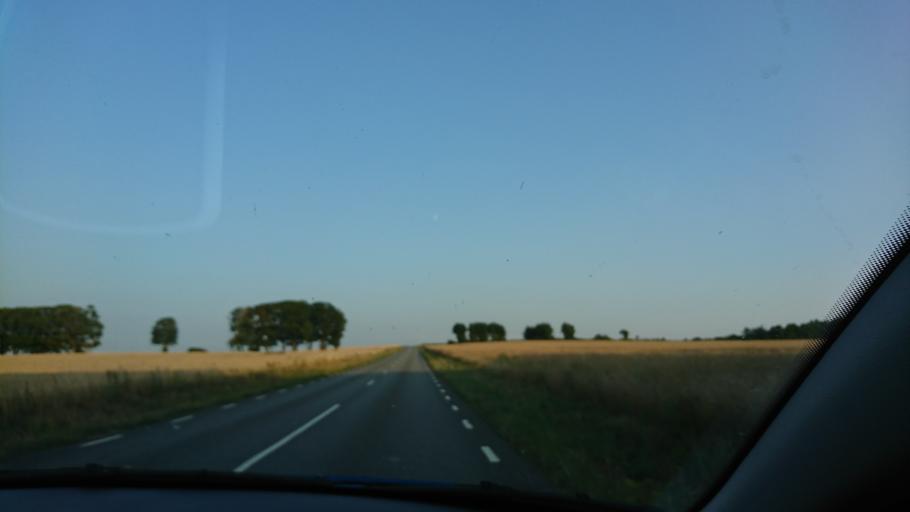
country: SE
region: Skane
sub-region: Simrishamns Kommun
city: Kivik
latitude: 55.7001
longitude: 14.1518
